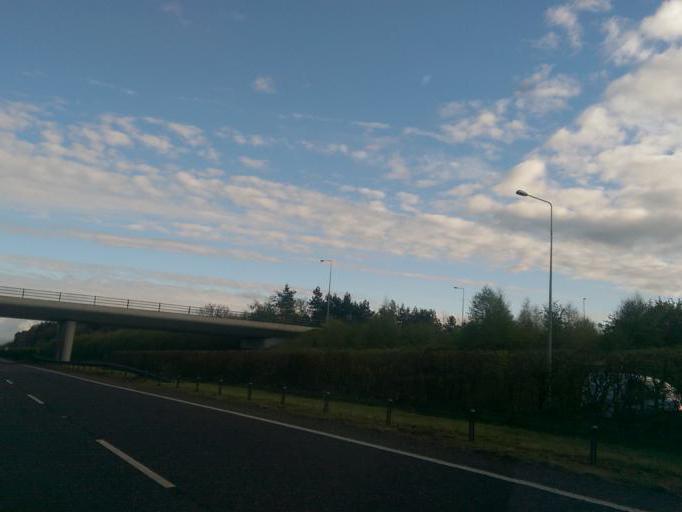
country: IE
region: Leinster
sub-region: Kildare
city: Kilcock
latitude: 53.3971
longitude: -6.6820
